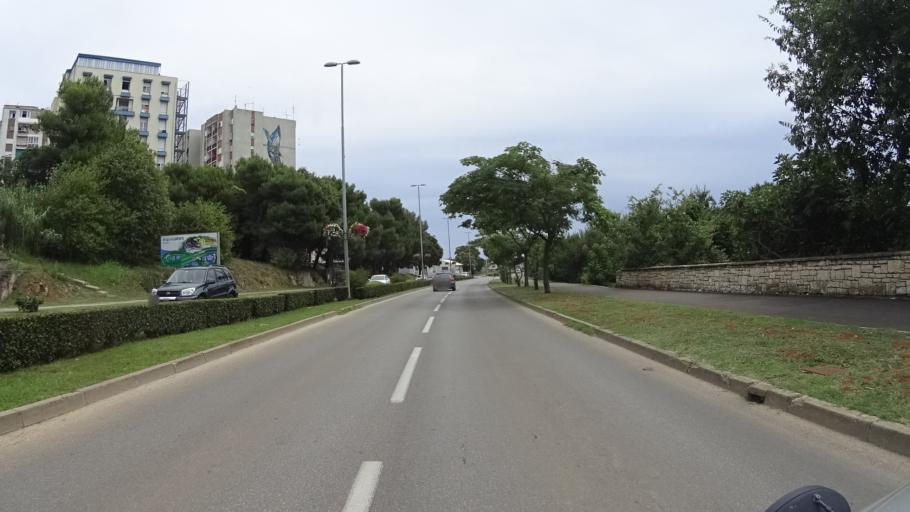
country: HR
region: Istarska
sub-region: Grad Pula
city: Pula
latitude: 44.8523
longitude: 13.8402
